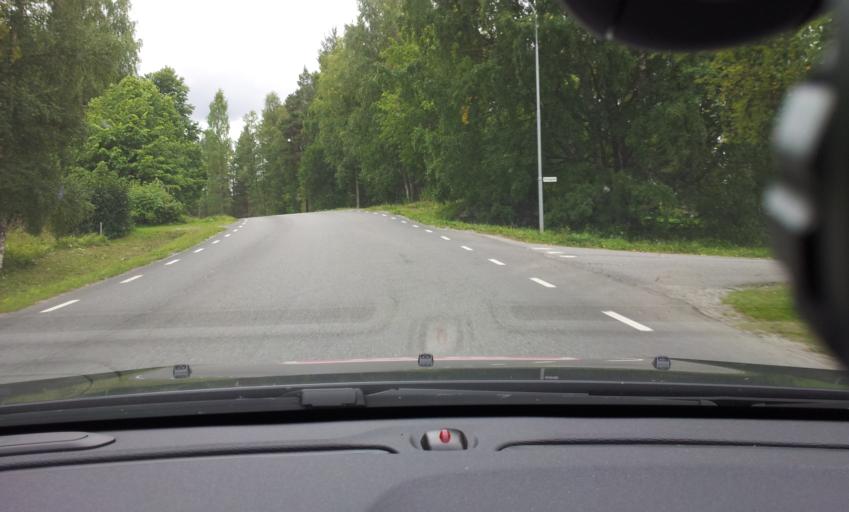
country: SE
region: Jaemtland
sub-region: Braecke Kommun
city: Braecke
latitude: 62.9707
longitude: 15.1680
